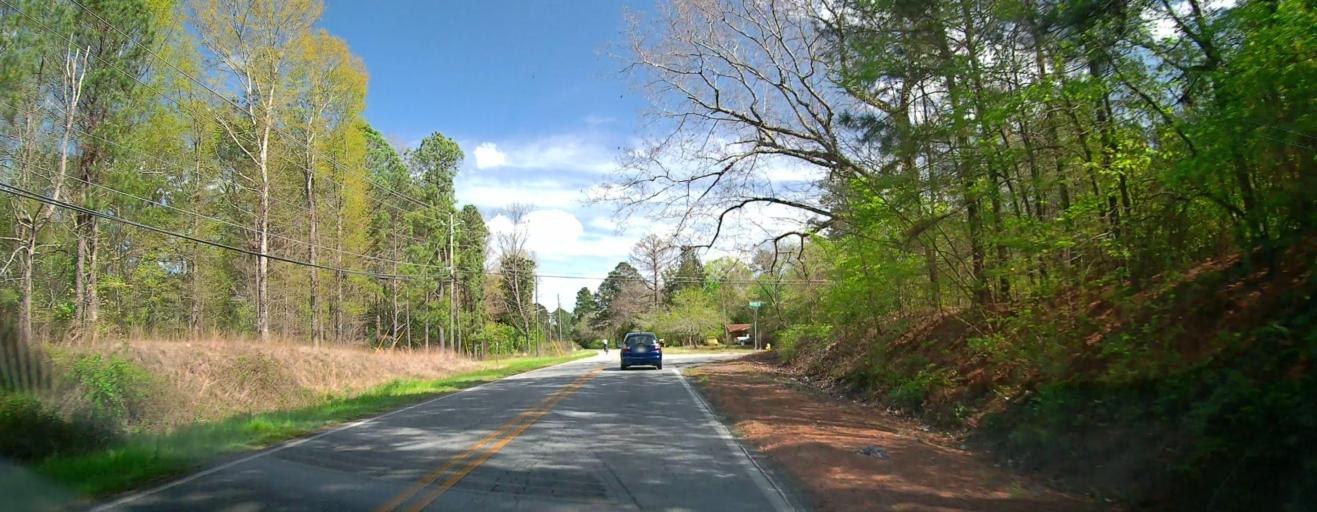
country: US
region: Georgia
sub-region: Bibb County
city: Macon
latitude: 32.8355
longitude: -83.5675
